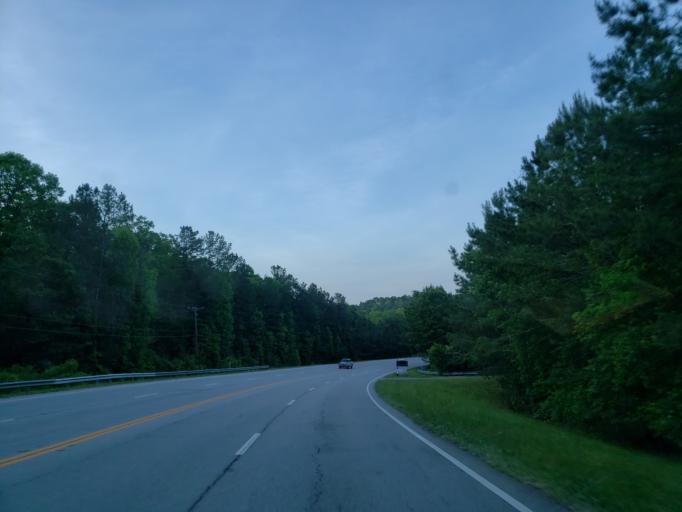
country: US
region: Georgia
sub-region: Fulton County
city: Chattahoochee Hills
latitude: 33.6515
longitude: -84.8225
